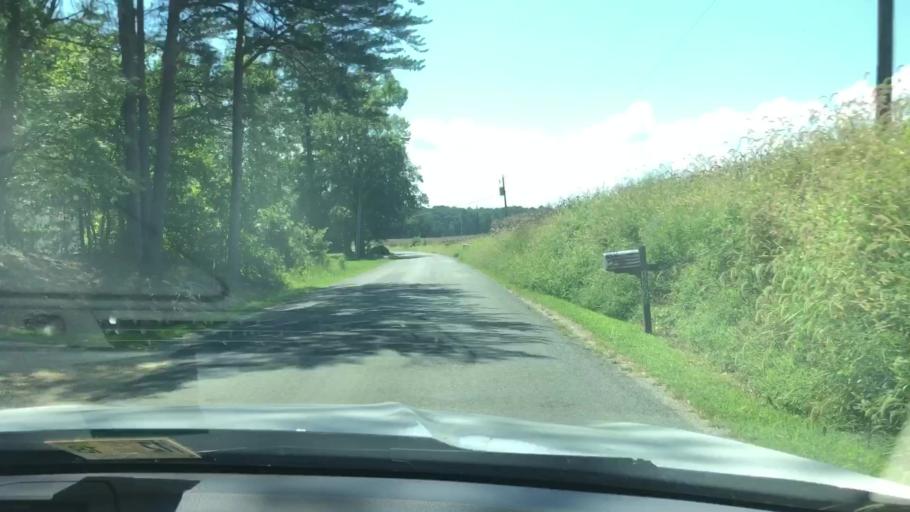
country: US
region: Virginia
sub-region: Charles City County
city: Charles City
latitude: 37.2815
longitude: -76.9637
